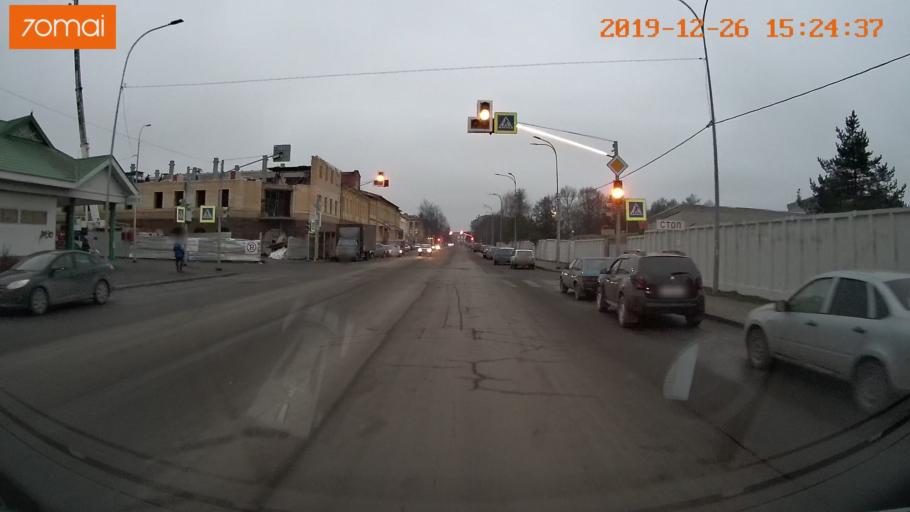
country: RU
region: Jaroslavl
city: Rybinsk
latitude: 58.0511
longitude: 38.8470
